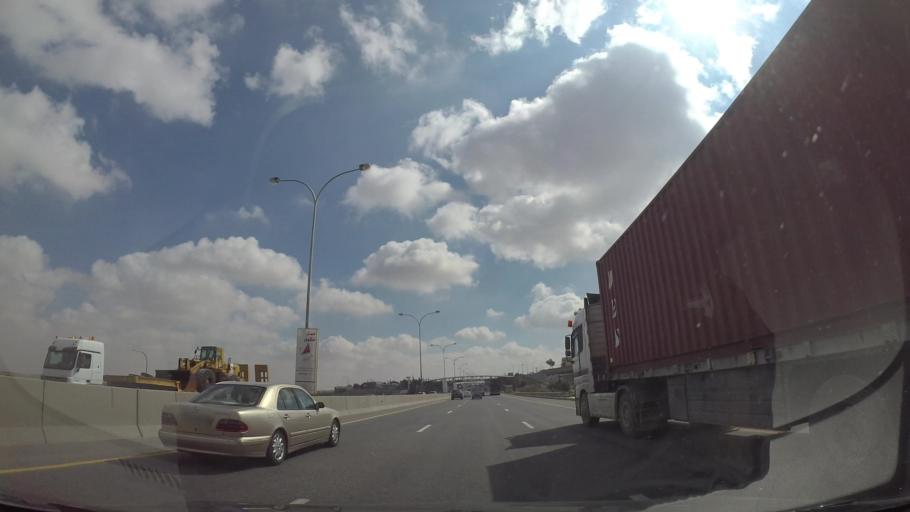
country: JO
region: Amman
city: Al Jizah
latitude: 31.7490
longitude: 35.9413
